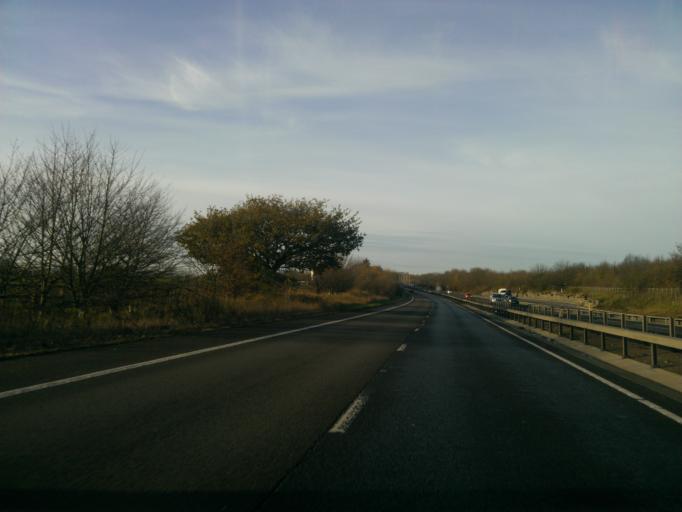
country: GB
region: England
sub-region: Essex
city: Witham
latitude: 51.7859
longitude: 0.6343
